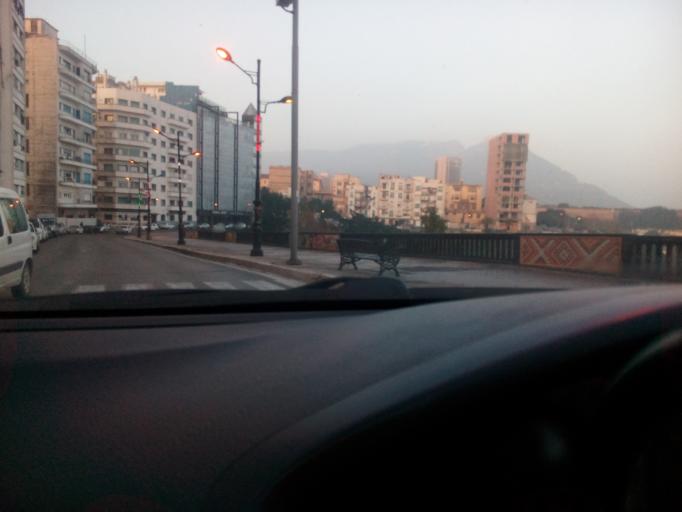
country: DZ
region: Oran
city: Oran
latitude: 35.7056
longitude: -0.6404
